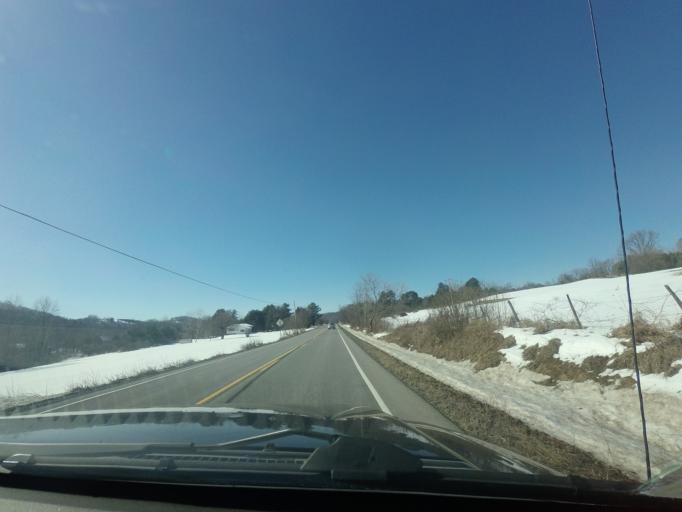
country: US
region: New York
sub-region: Washington County
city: Greenwich
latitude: 43.1004
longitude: -73.4408
